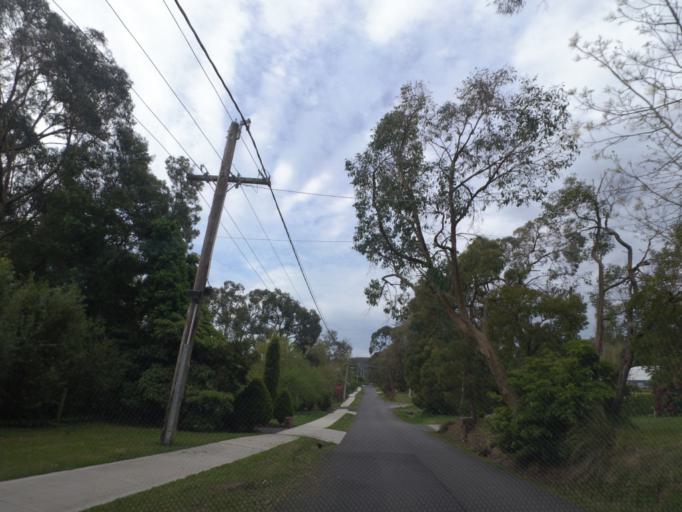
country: AU
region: Victoria
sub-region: Yarra Ranges
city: Montrose
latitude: -37.8131
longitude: 145.3539
